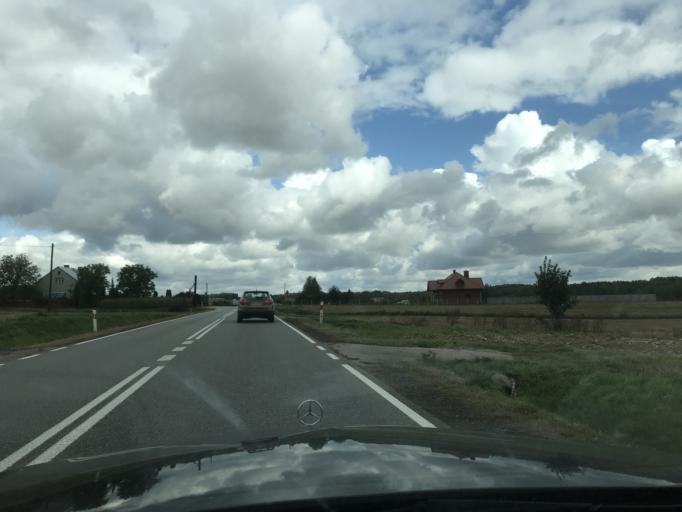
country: PL
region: Lublin Voivodeship
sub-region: Powiat janowski
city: Modliborzyce
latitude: 50.7937
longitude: 22.3179
